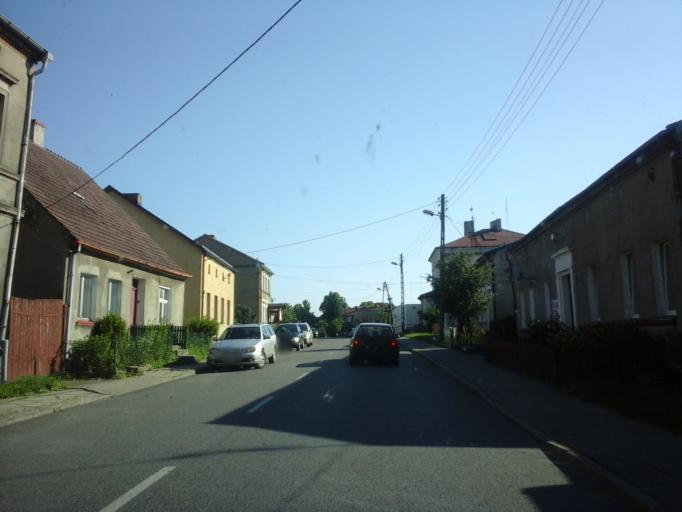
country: PL
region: West Pomeranian Voivodeship
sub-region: Powiat lobeski
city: Dobra
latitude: 53.5843
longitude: 15.3075
